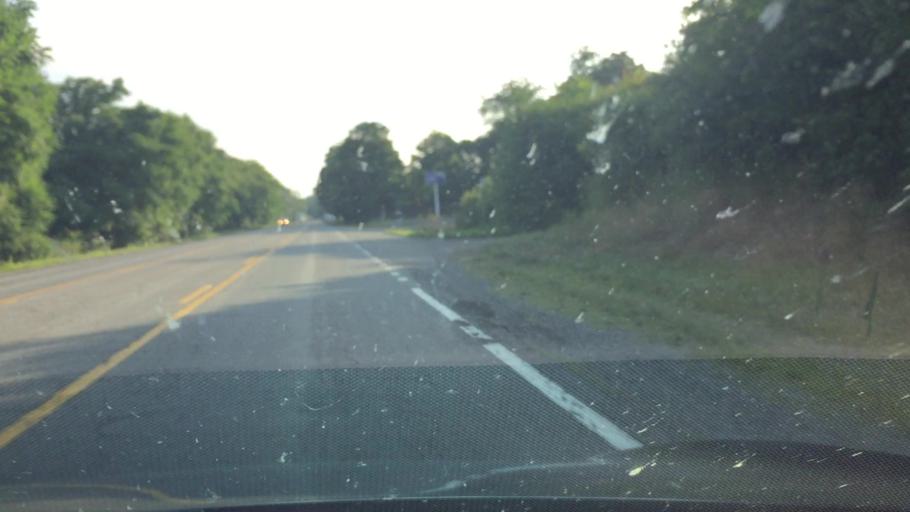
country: US
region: Virginia
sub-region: Pulaski County
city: Dublin
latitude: 37.1205
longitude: -80.6587
